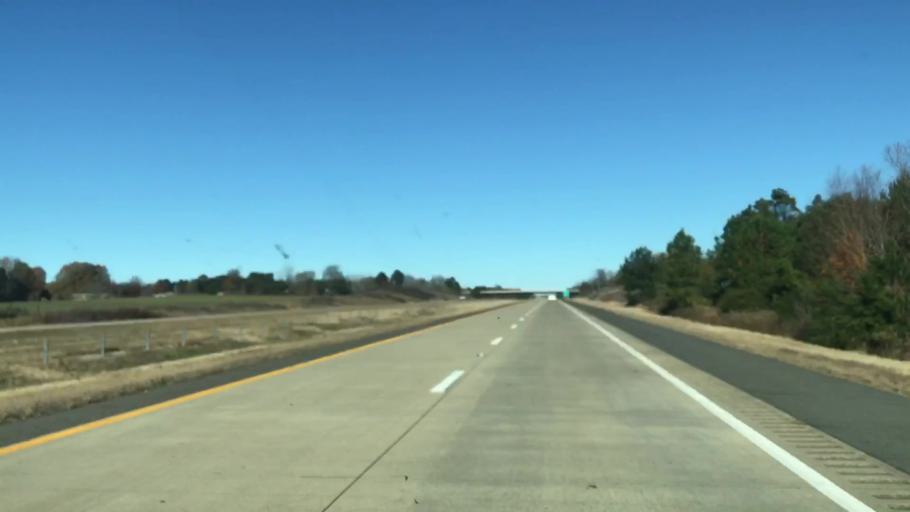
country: US
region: Texas
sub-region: Bowie County
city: Texarkana
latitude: 33.3118
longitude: -93.9408
